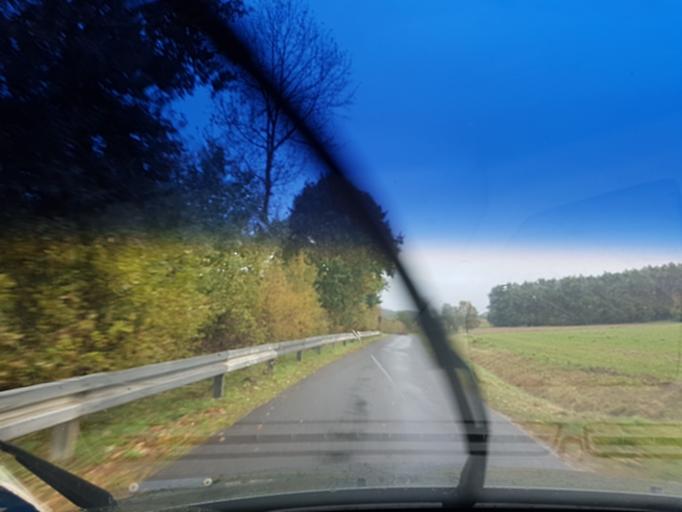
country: DE
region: Bavaria
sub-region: Regierungsbezirk Mittelfranken
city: Wachenroth
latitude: 49.7631
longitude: 10.6744
